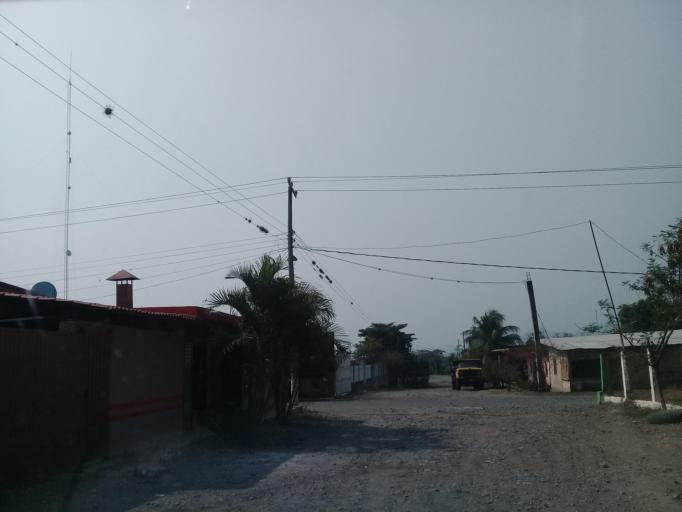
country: MX
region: Oaxaca
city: Acatlan de Perez Figueroa
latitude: 18.6065
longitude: -96.5762
